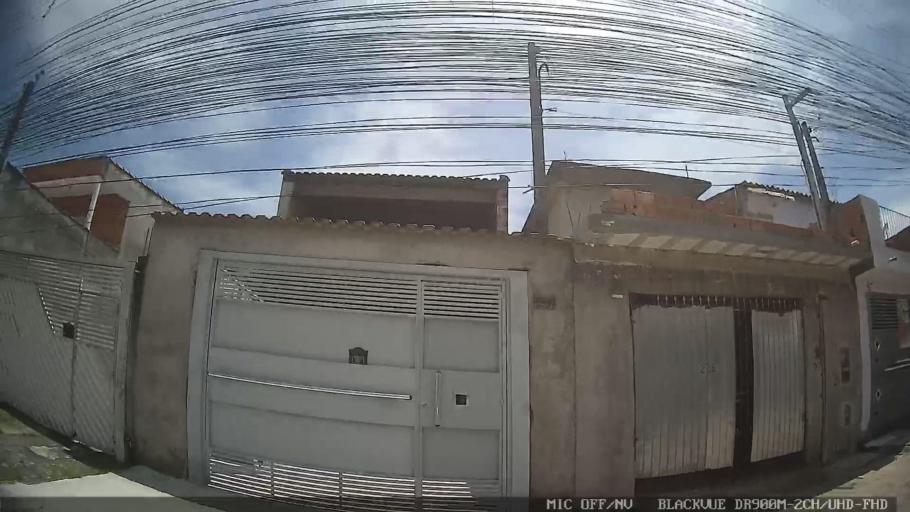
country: BR
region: Sao Paulo
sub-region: Suzano
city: Suzano
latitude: -23.5236
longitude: -46.3090
